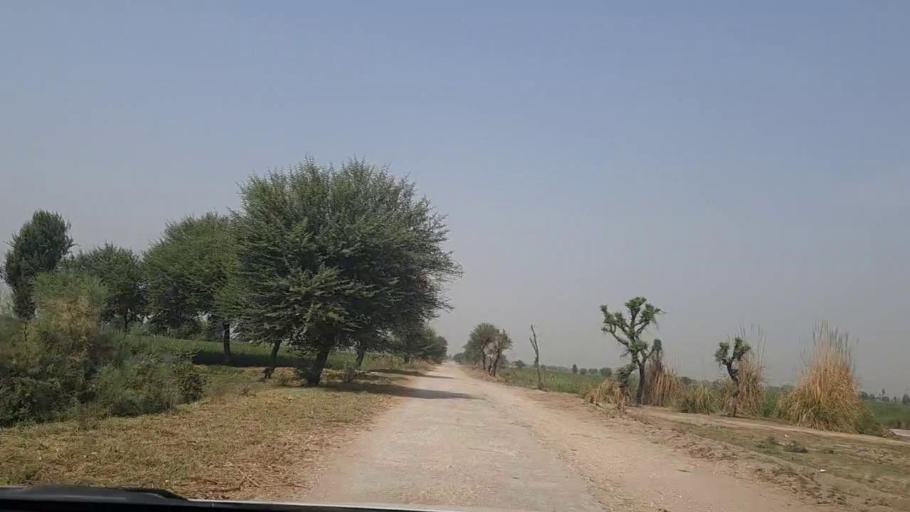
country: PK
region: Sindh
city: Mirpur Khas
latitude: 25.6118
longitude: 69.2010
